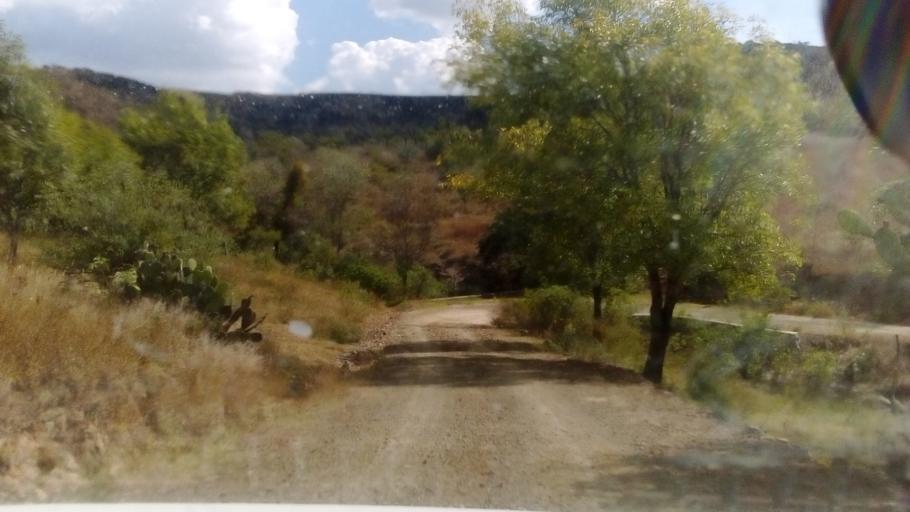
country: MX
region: Guanajuato
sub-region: Silao de la Victoria
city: San Francisco (Banos de Agua Caliente)
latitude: 21.1815
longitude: -101.4558
